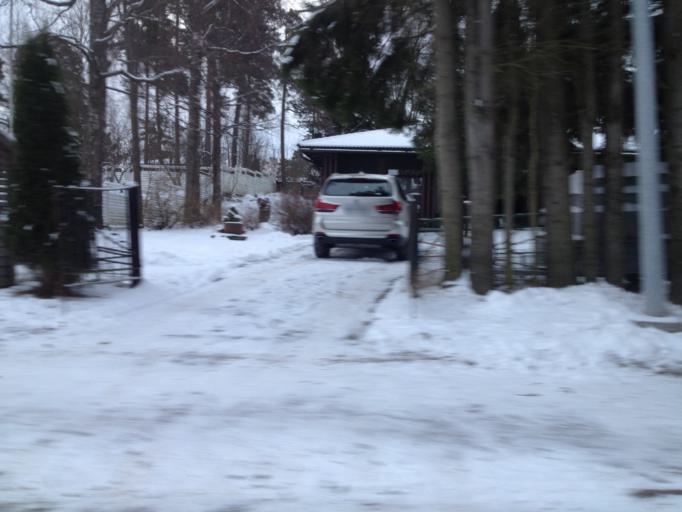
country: FI
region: Uusimaa
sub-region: Helsinki
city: Vantaa
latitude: 60.2019
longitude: 25.0745
